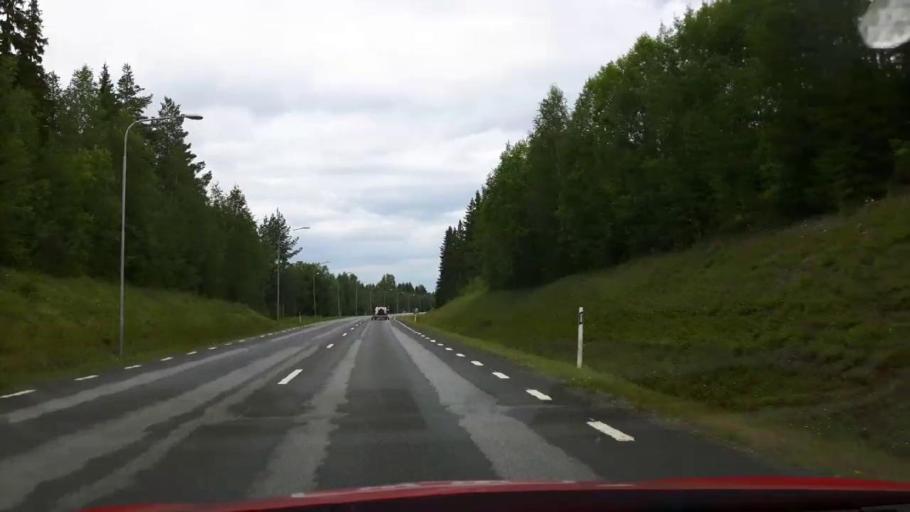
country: SE
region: Jaemtland
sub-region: Stroemsunds Kommun
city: Stroemsund
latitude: 63.6687
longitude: 15.3914
